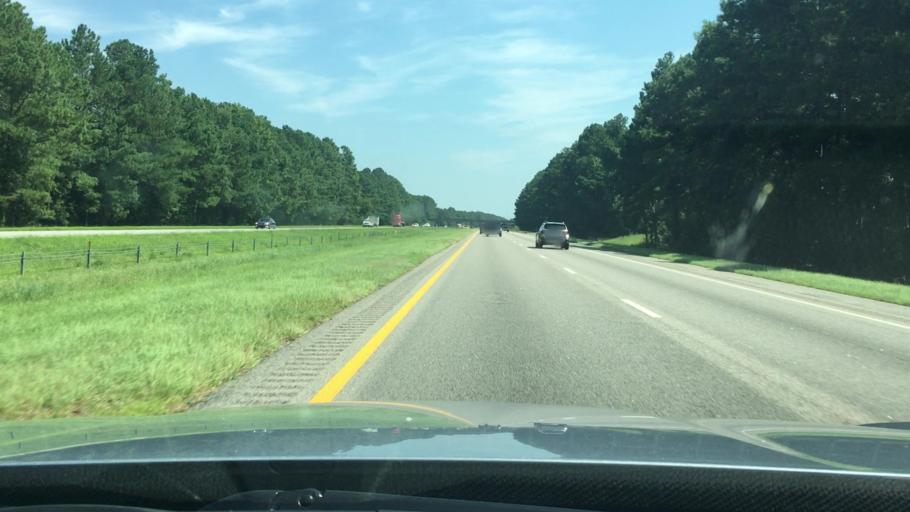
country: US
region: South Carolina
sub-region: Florence County
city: Timmonsville
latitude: 33.9390
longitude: -80.0633
